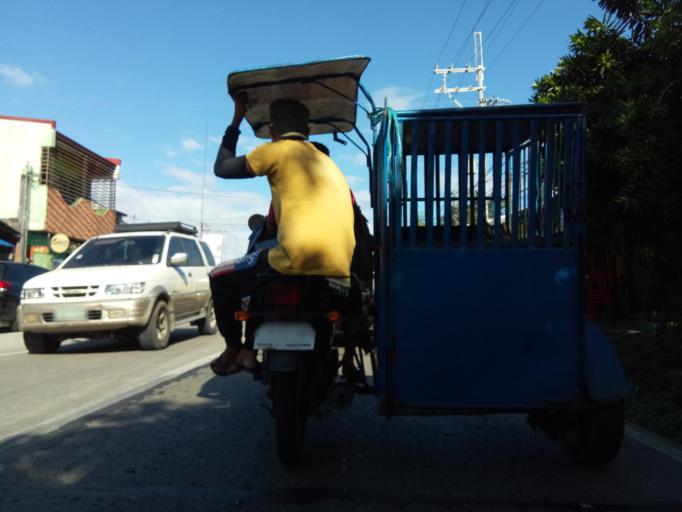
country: PH
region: Calabarzon
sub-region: Province of Cavite
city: Dasmarinas
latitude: 14.3503
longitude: 120.9728
